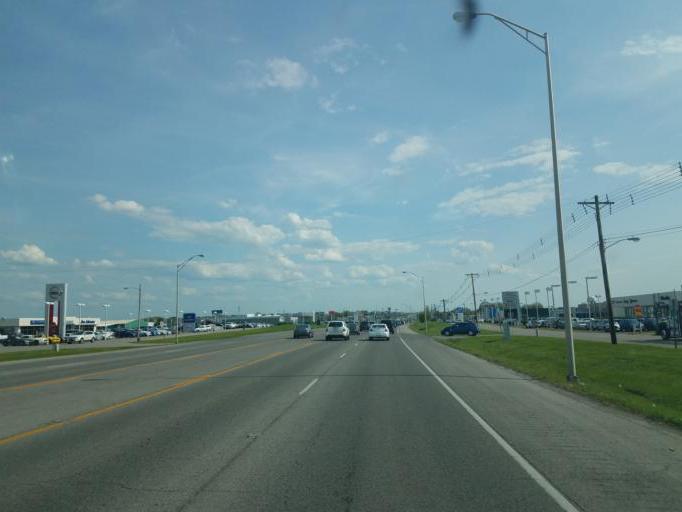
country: US
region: Kentucky
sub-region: Warren County
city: Bowling Green
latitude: 36.9584
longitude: -86.4288
